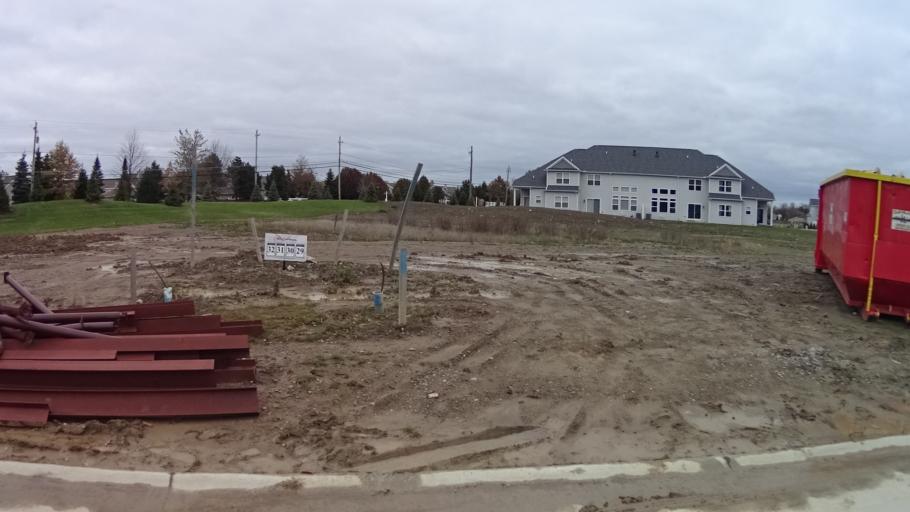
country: US
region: Ohio
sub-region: Lorain County
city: Avon Lake
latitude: 41.4871
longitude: -82.0366
